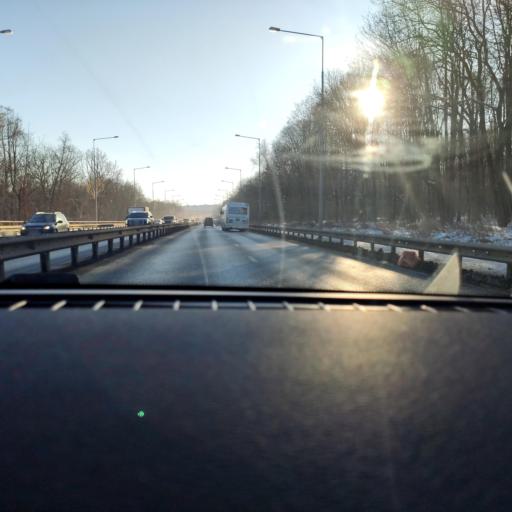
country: RU
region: Samara
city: Volzhskiy
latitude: 53.3610
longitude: 50.2051
